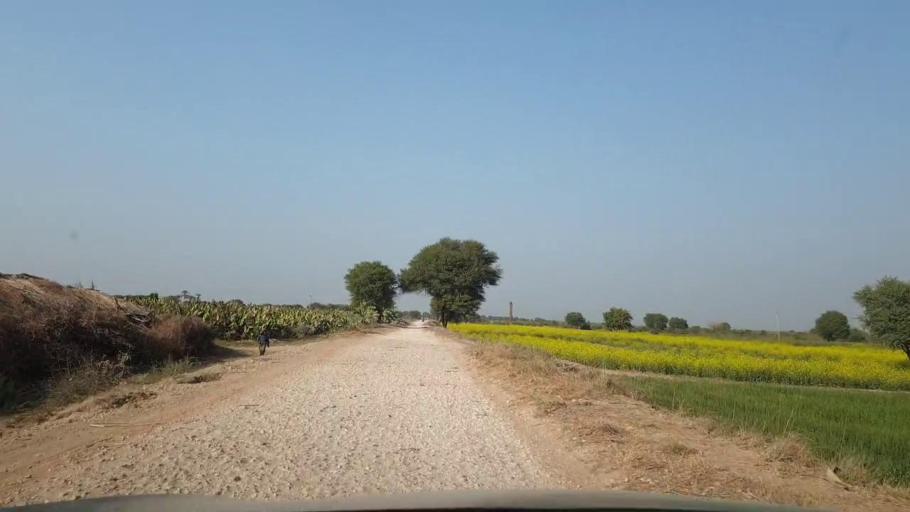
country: PK
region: Sindh
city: Tando Allahyar
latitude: 25.5711
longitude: 68.7951
